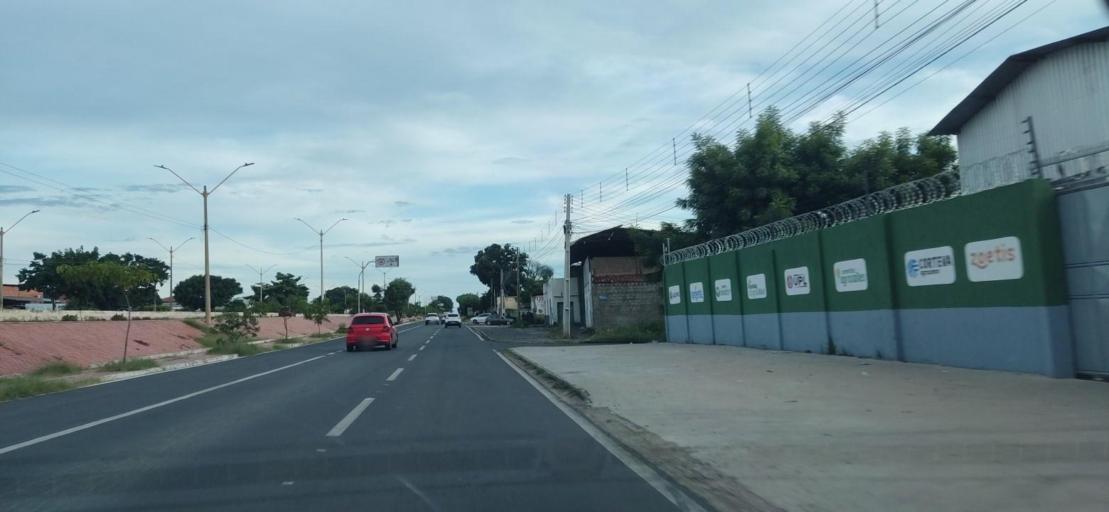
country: BR
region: Piaui
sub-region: Teresina
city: Teresina
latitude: -5.1305
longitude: -42.7922
